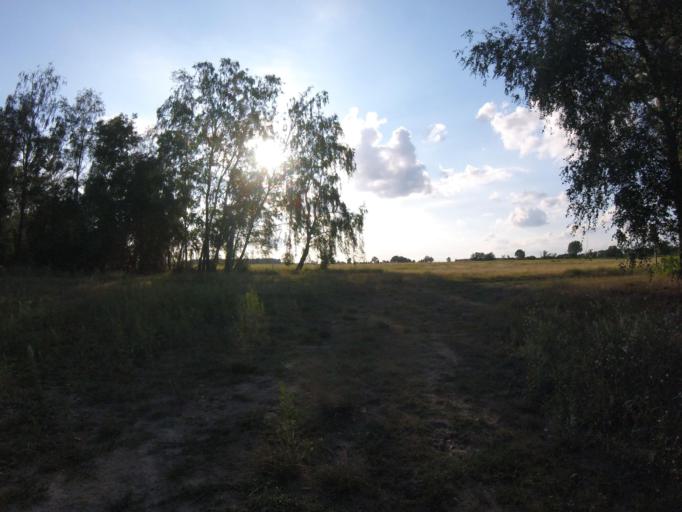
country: DE
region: Brandenburg
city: Mittenwalde
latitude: 52.2782
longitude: 13.5094
